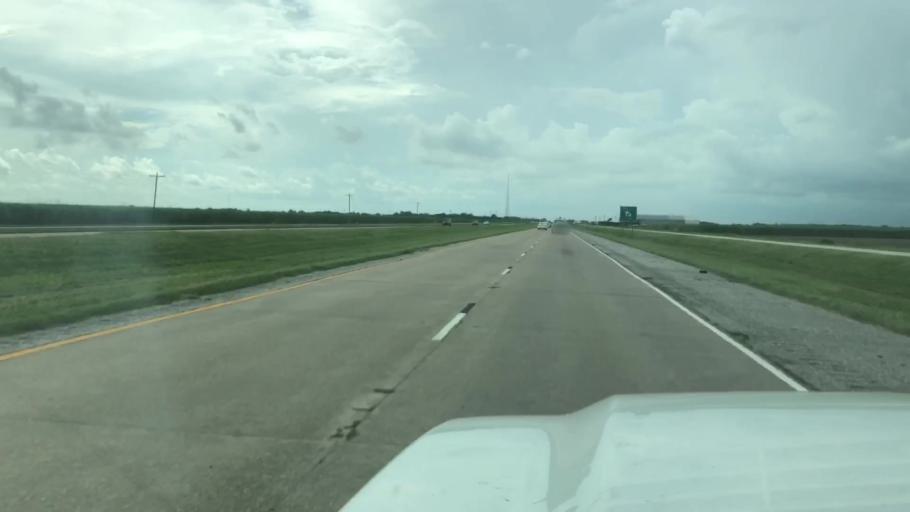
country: US
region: Louisiana
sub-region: Iberia Parish
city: Jeanerette
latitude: 29.9070
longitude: -91.7093
